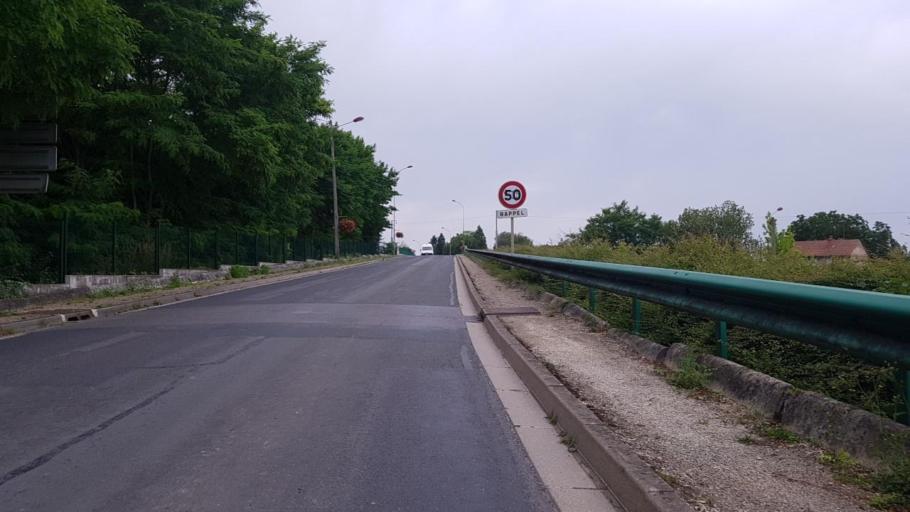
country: FR
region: Champagne-Ardenne
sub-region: Departement de la Marne
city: Pargny-sur-Saulx
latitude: 48.7684
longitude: 4.8432
